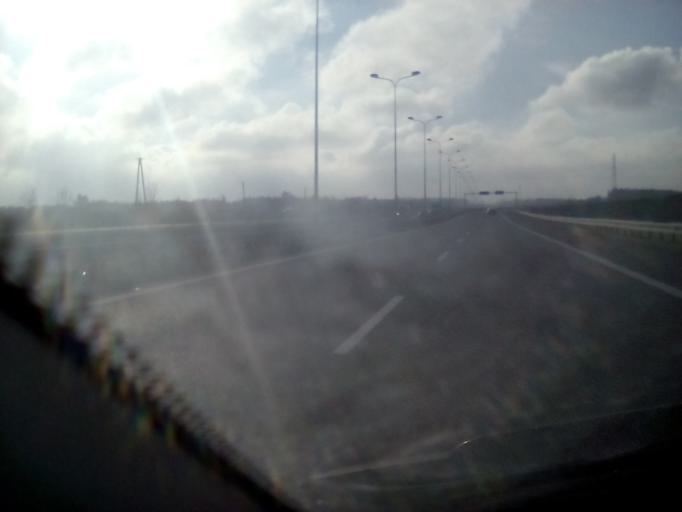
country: PL
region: Masovian Voivodeship
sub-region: Powiat grojecki
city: Goszczyn
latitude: 51.7412
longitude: 20.9122
